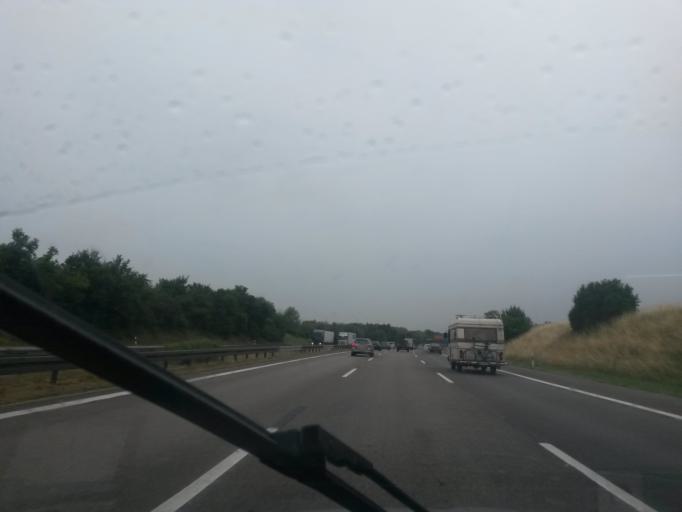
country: DE
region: Bavaria
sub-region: Upper Bavaria
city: Hepberg
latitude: 48.8117
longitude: 11.4662
